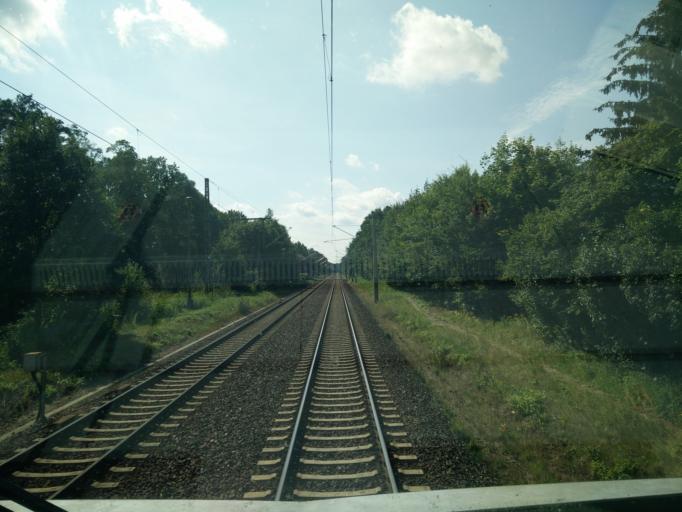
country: DE
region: Brandenburg
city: Konigs Wusterhausen
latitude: 52.2804
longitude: 13.6325
